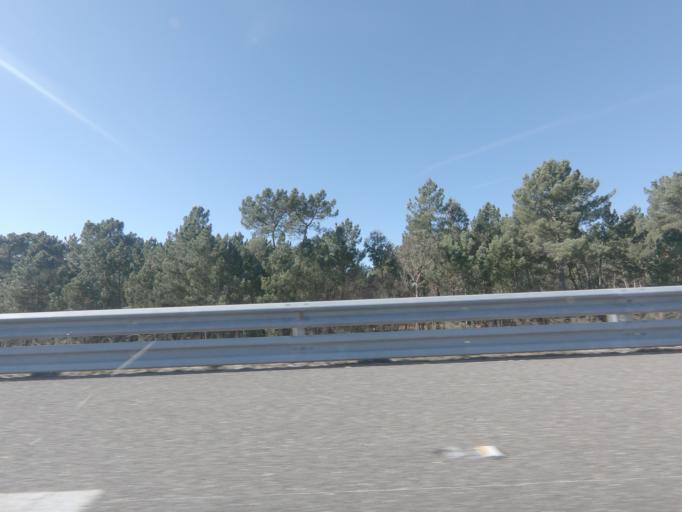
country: ES
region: Galicia
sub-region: Provincia de Ourense
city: Maside
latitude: 42.4350
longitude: -8.0182
